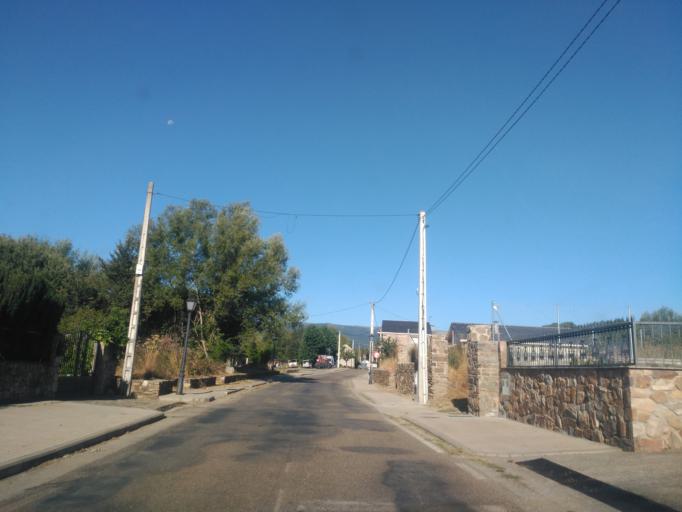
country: ES
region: Castille and Leon
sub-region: Provincia de Zamora
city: Galende
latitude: 42.0867
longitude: -6.6582
